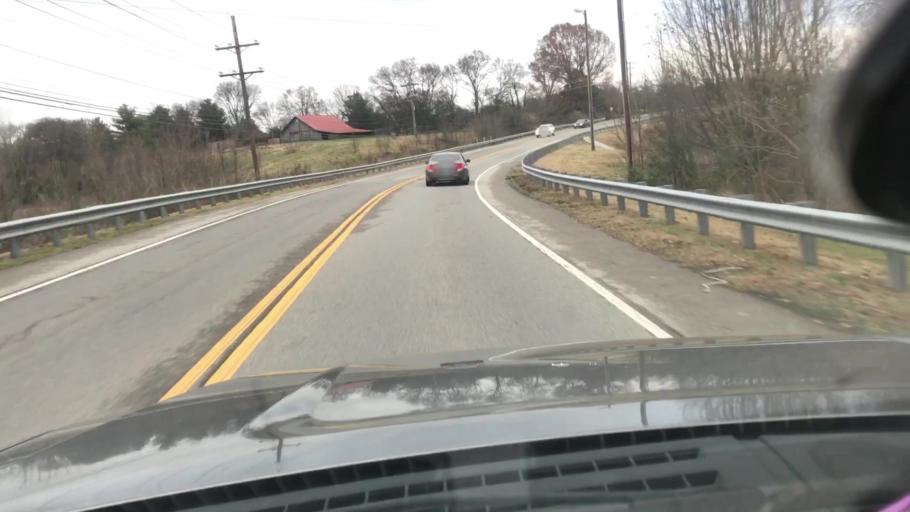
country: US
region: Tennessee
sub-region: Williamson County
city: Brentwood Estates
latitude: 35.9690
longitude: -86.7767
